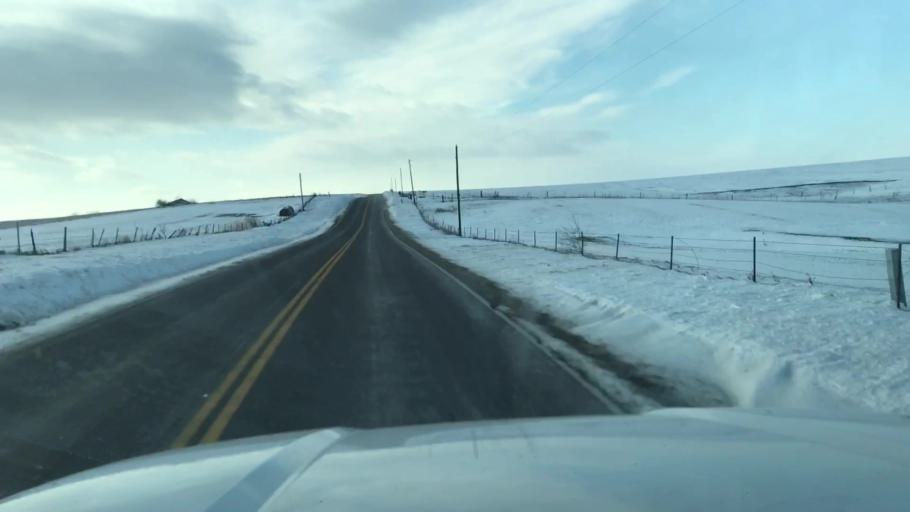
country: US
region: Missouri
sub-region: Nodaway County
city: Maryville
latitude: 40.2010
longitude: -94.9039
